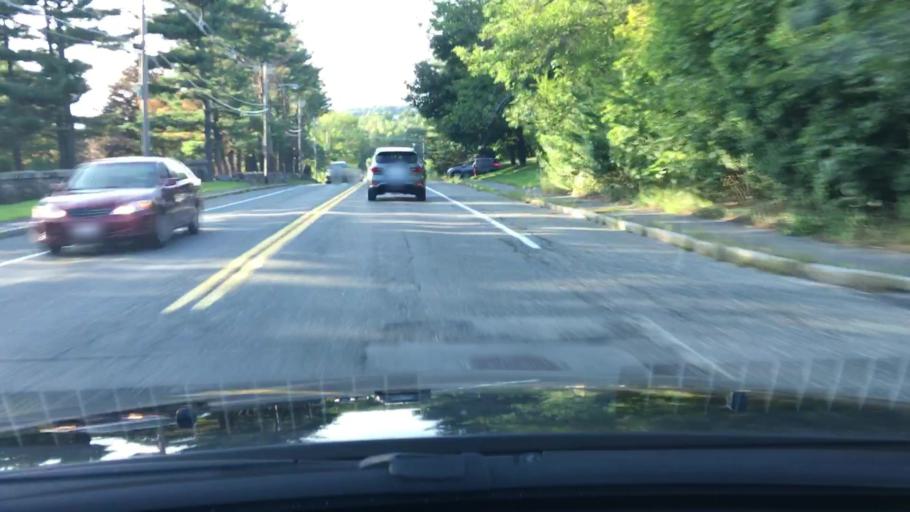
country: US
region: Massachusetts
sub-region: Worcester County
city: Shrewsbury
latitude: 42.3000
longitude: -71.7146
